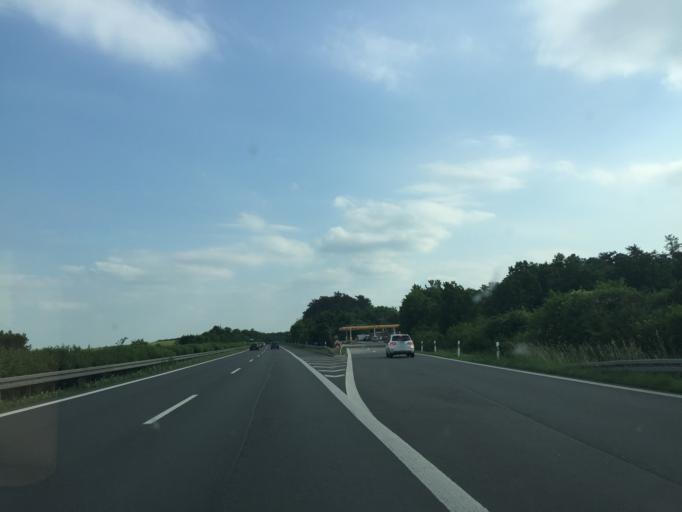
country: DE
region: Baden-Wuerttemberg
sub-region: Regierungsbezirk Stuttgart
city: Grunsfeld
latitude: 49.6304
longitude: 9.7295
